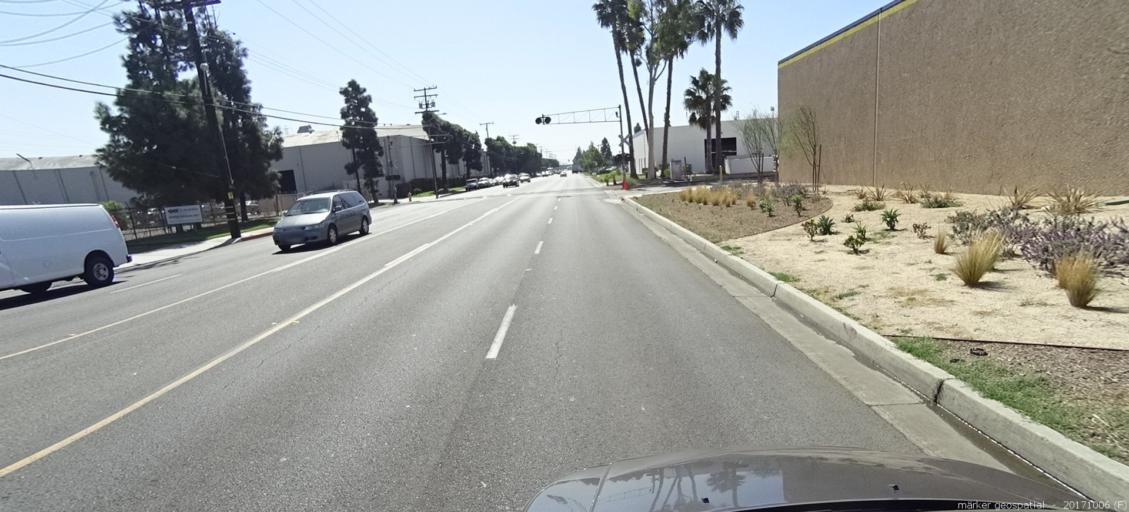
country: US
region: California
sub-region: Orange County
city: Stanton
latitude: 33.7838
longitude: -118.0016
